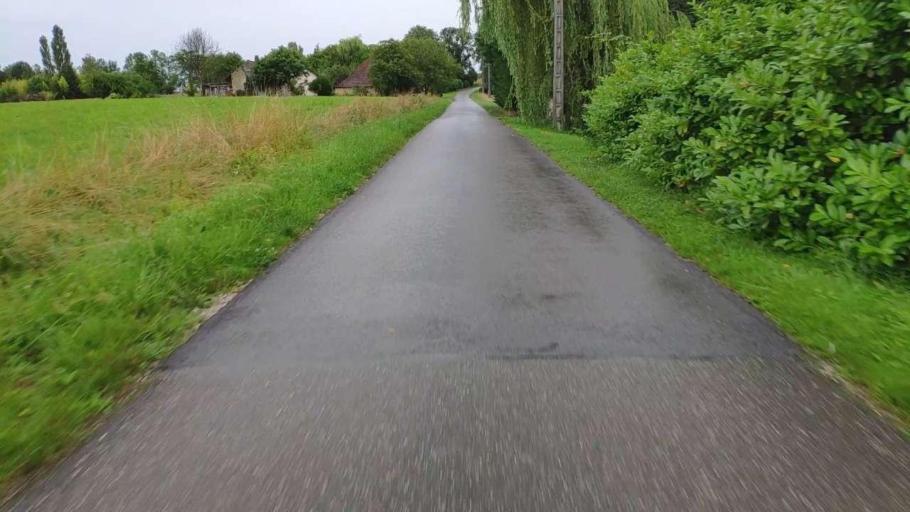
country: FR
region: Franche-Comte
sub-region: Departement du Jura
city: Chaussin
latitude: 46.8806
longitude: 5.4150
